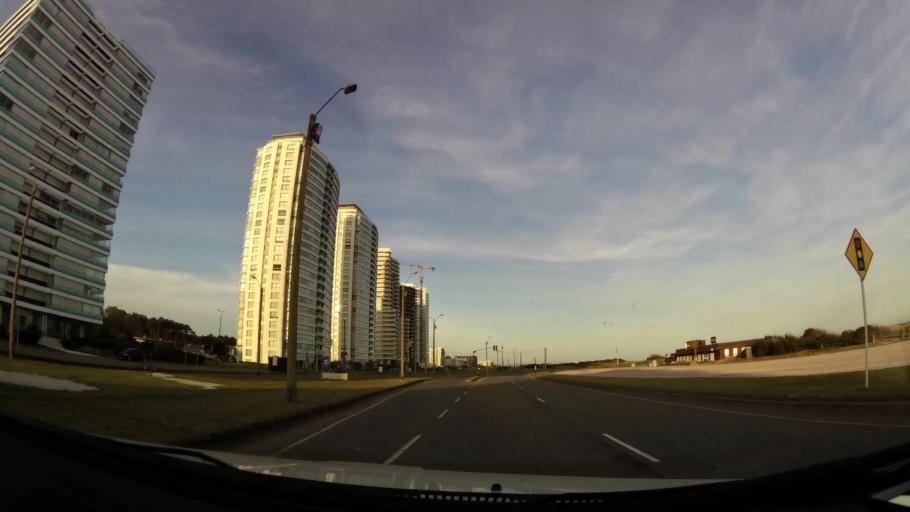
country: UY
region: Maldonado
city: Punta del Este
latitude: -34.9488
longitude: -54.9255
